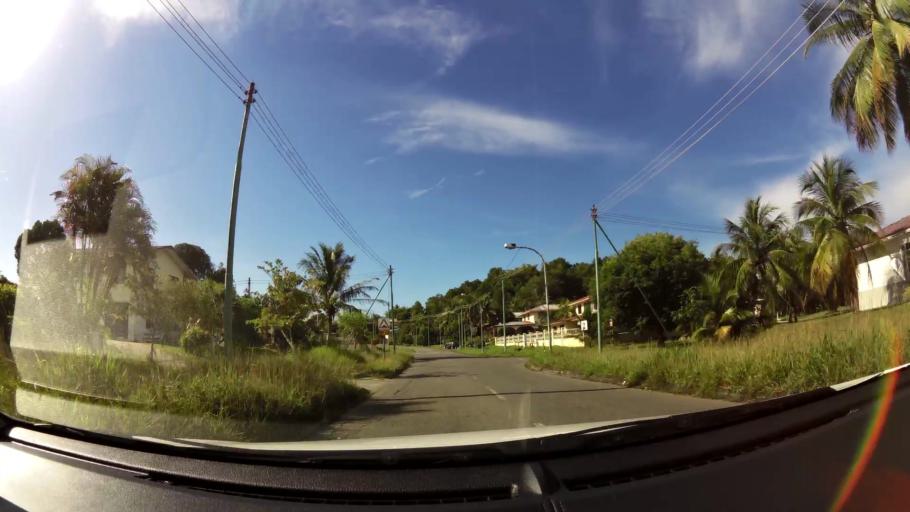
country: BN
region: Brunei and Muara
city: Bandar Seri Begawan
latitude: 4.9635
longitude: 114.9547
